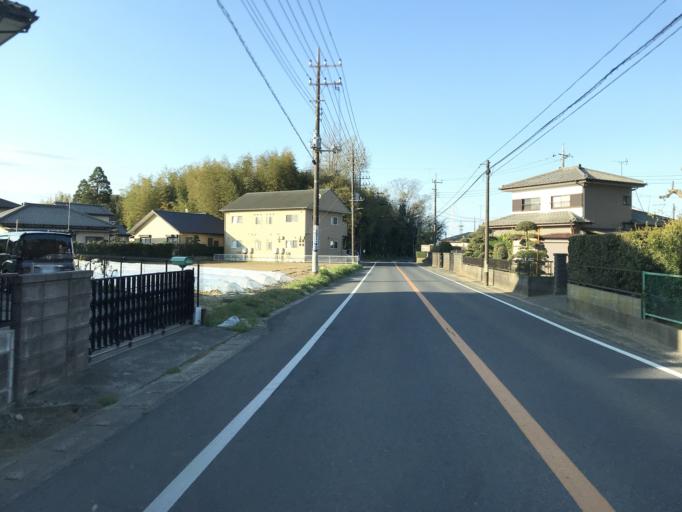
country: JP
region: Chiba
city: Yokaichiba
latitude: 35.7107
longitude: 140.5600
